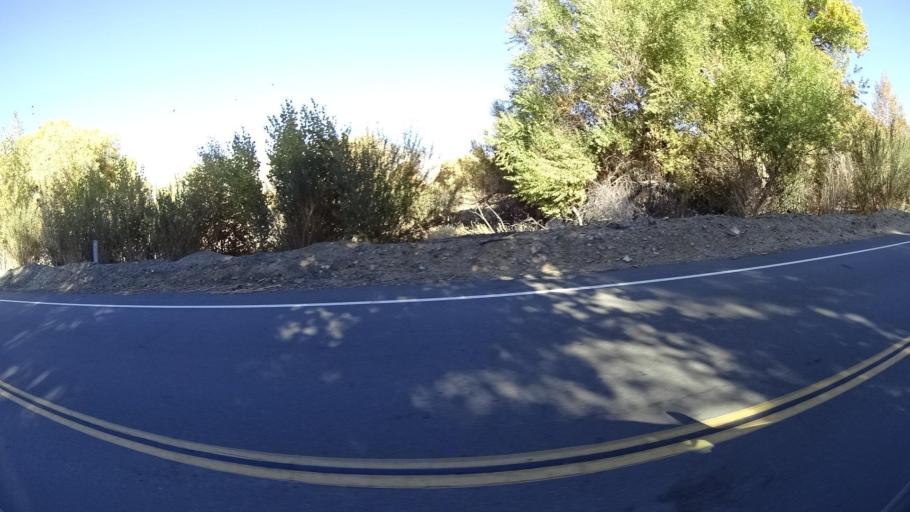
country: US
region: California
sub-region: Kern County
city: Weldon
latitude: 35.6703
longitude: -118.3240
